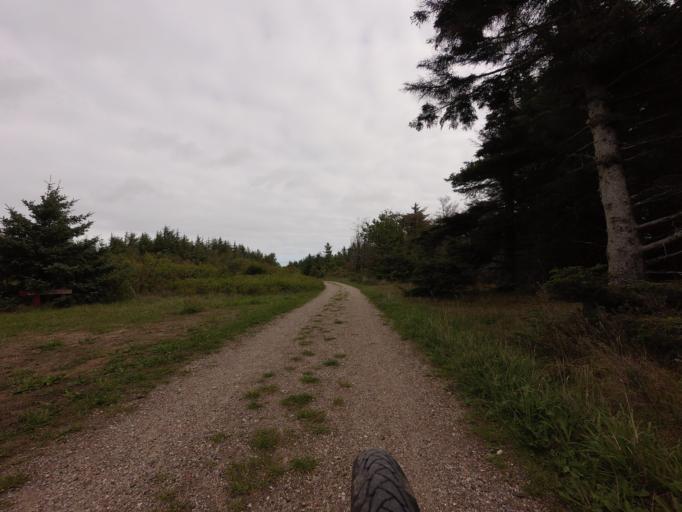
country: DK
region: North Denmark
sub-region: Hjorring Kommune
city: Hirtshals
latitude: 57.5543
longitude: 9.9247
